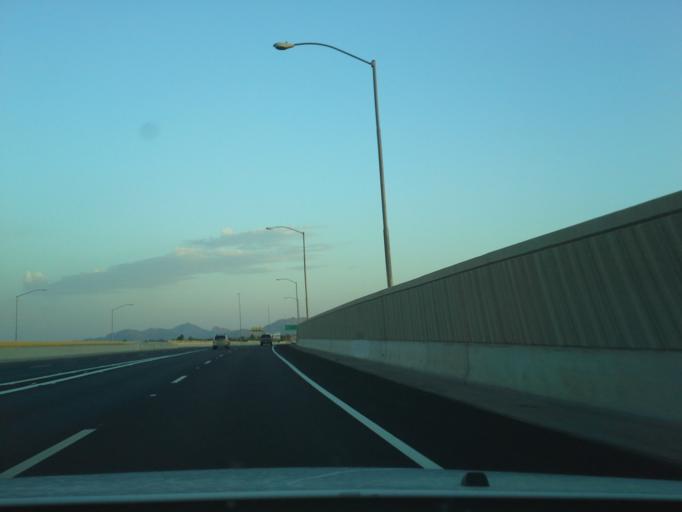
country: US
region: Arizona
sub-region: Maricopa County
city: Paradise Valley
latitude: 33.6654
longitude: -112.0002
